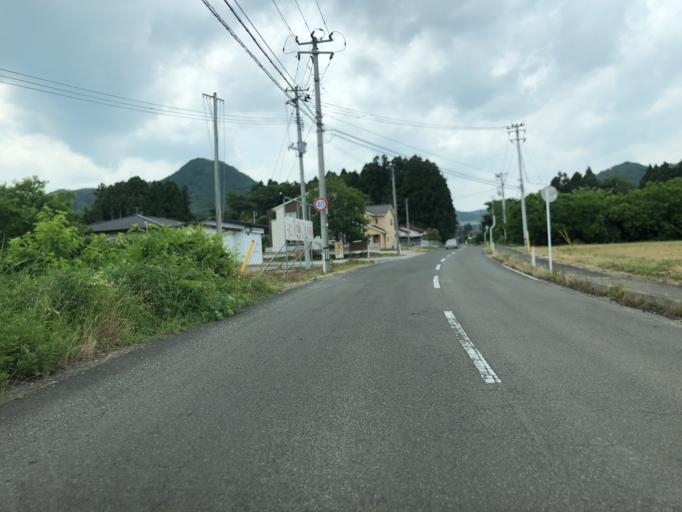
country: JP
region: Miyagi
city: Marumori
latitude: 37.8209
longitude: 140.8841
